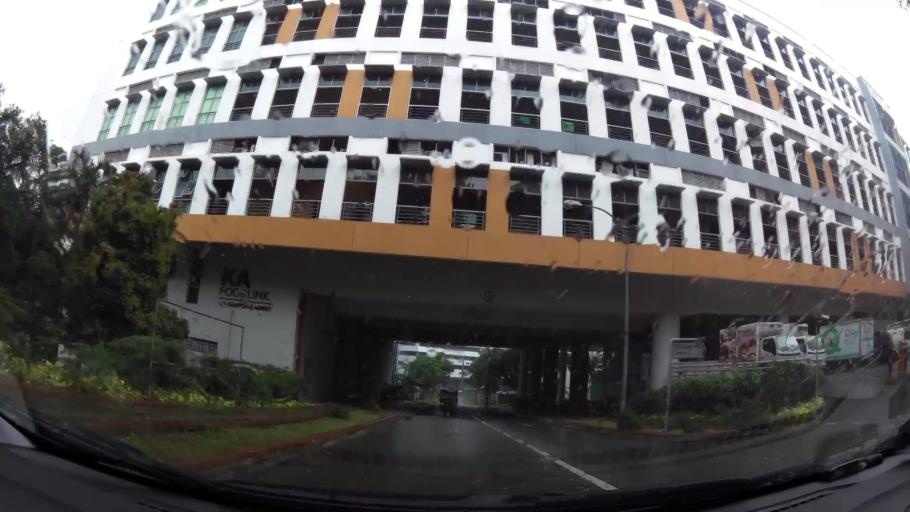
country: SG
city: Singapore
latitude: 1.3365
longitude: 103.8827
